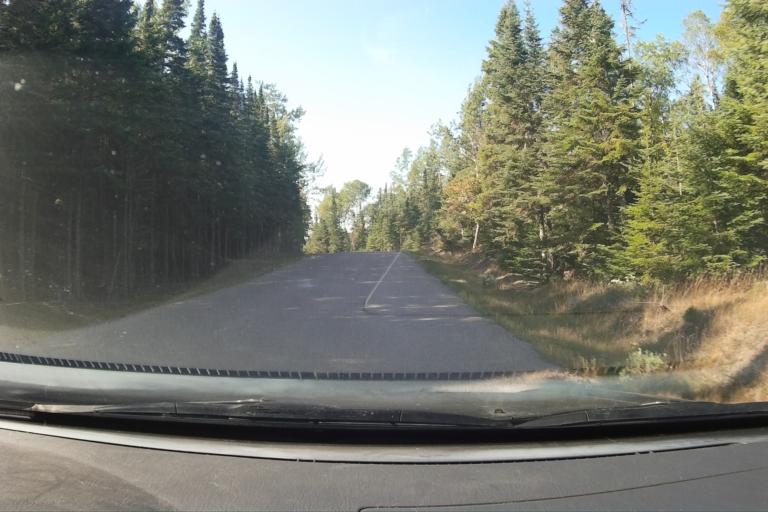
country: CA
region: Ontario
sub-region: Thunder Bay District
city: Thunder Bay
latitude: 48.3399
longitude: -88.8222
